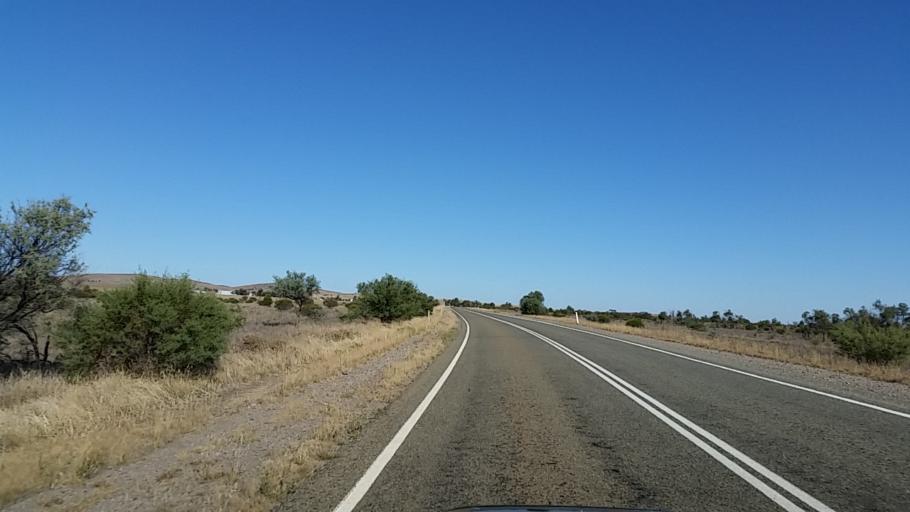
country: AU
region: South Australia
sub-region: Peterborough
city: Peterborough
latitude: -32.5300
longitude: 138.5523
